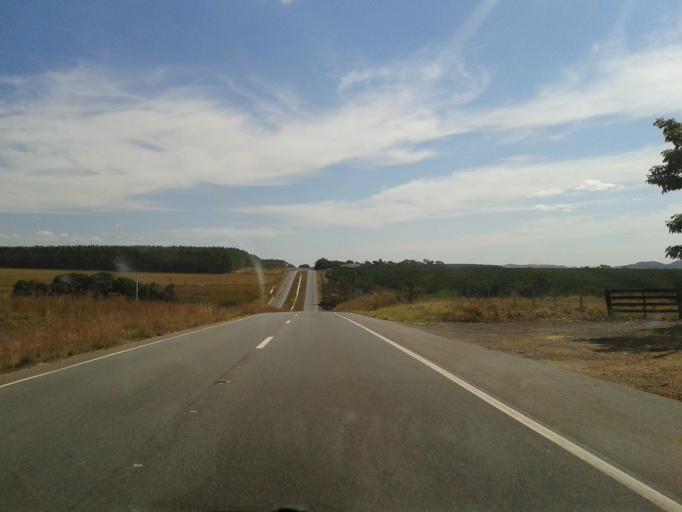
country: BR
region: Goias
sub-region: Itaberai
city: Itaberai
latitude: -16.0092
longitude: -49.9396
